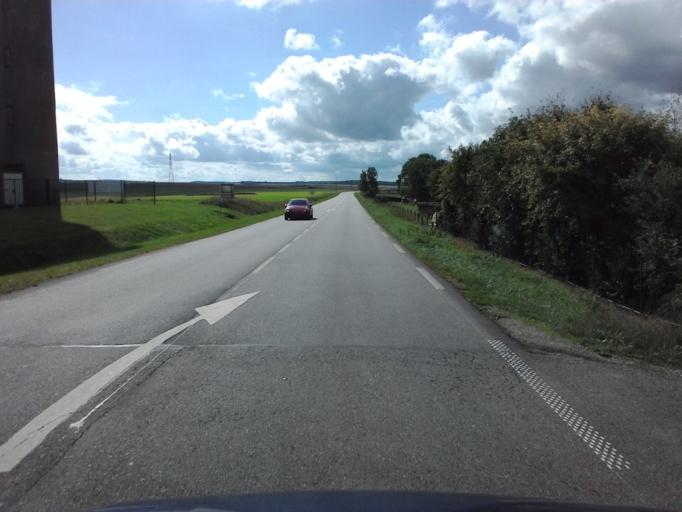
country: FR
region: Lorraine
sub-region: Departement de Meurthe-et-Moselle
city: Colombey-les-Belles
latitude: 48.4820
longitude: 5.8477
